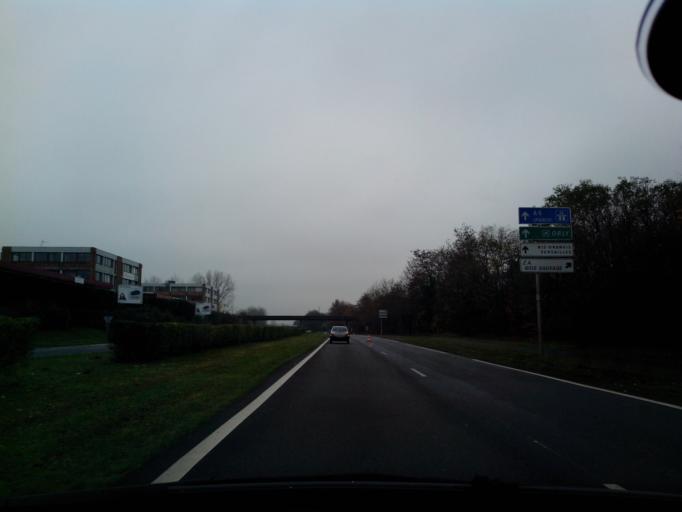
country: FR
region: Ile-de-France
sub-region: Departement de l'Essonne
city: Evry
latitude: 48.6365
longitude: 2.4335
